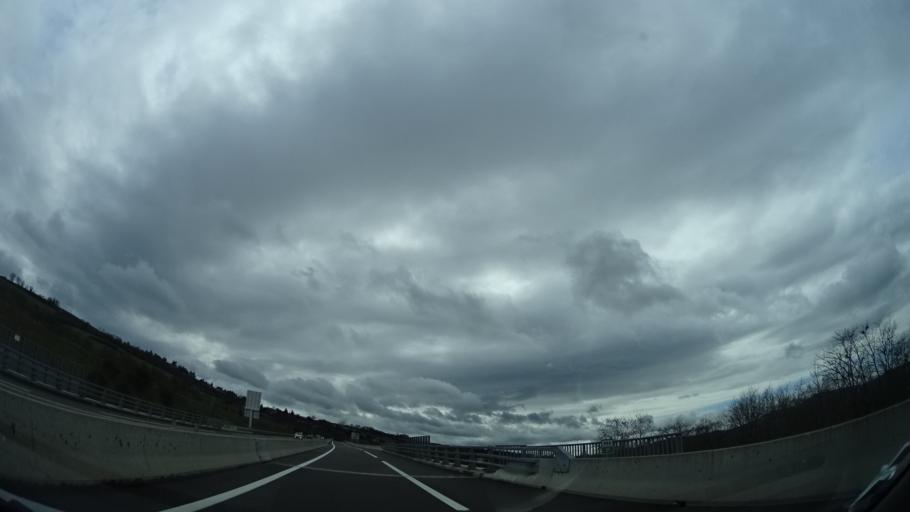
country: FR
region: Rhone-Alpes
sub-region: Departement du Rhone
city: Saint-Germain-Nuelles
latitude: 45.8440
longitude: 4.6400
